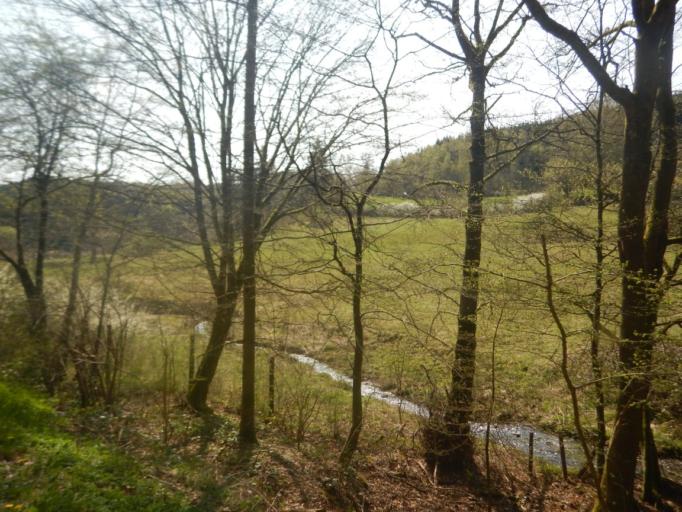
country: LU
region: Diekirch
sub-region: Canton de Clervaux
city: Clervaux
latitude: 50.0405
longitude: 6.0131
